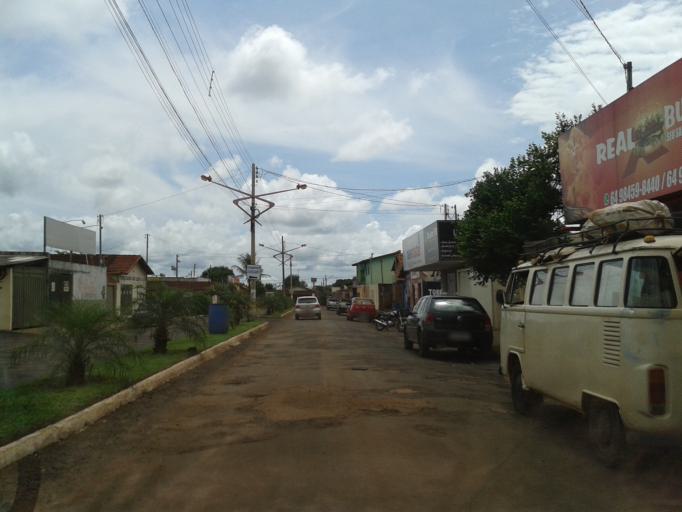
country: BR
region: Goias
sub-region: Buriti Alegre
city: Buriti Alegre
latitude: -18.1309
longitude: -49.0422
